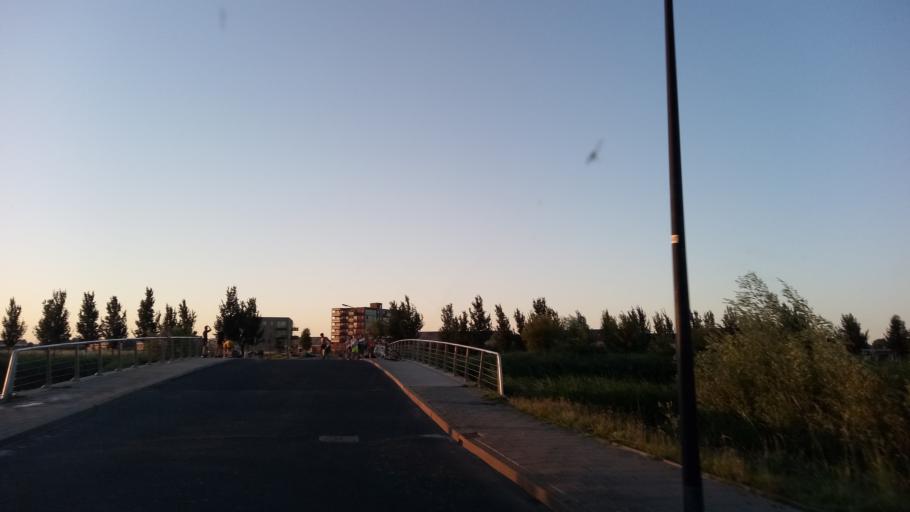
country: NL
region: North Holland
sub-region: Gemeente Langedijk
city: Broek op Langedijk
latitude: 52.6500
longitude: 4.8053
